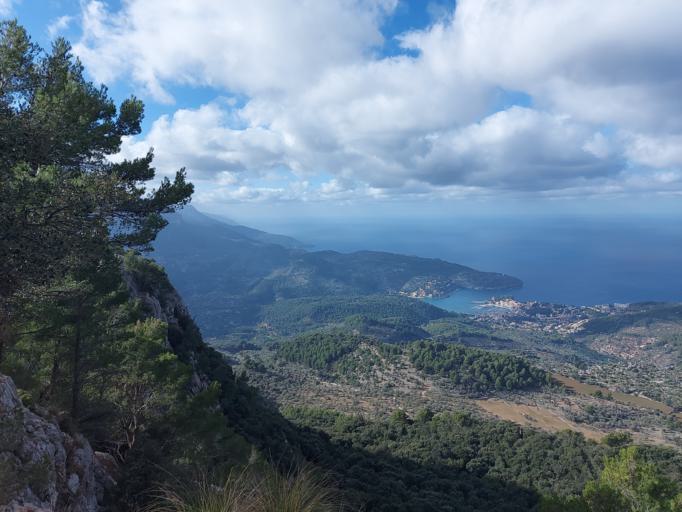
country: ES
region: Balearic Islands
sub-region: Illes Balears
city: Fornalutx
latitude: 39.7983
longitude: 2.7352
